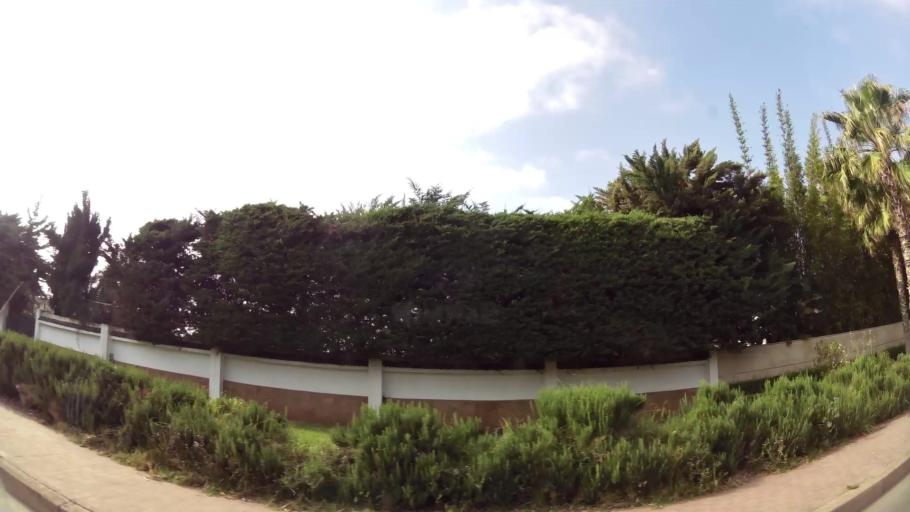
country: MA
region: Rabat-Sale-Zemmour-Zaer
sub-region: Rabat
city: Rabat
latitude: 33.9598
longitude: -6.8410
